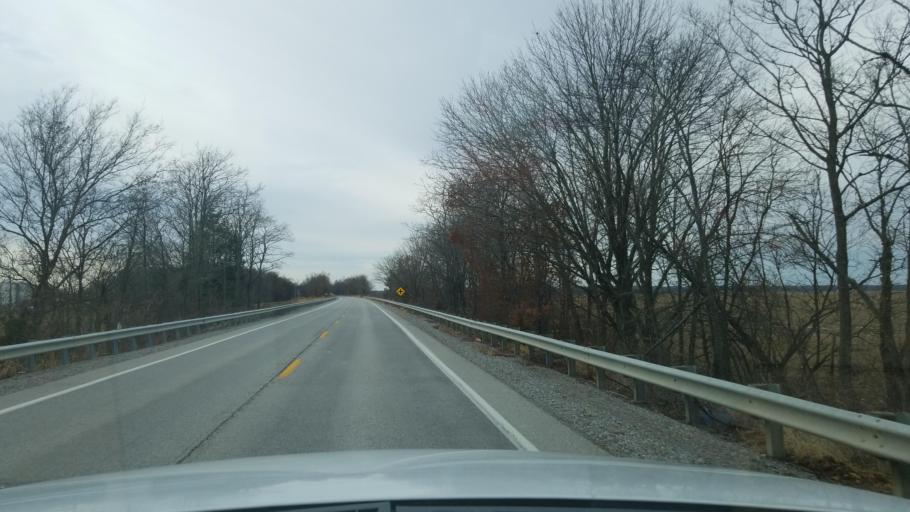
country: US
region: Illinois
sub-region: White County
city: Carmi
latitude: 37.9388
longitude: -88.0724
